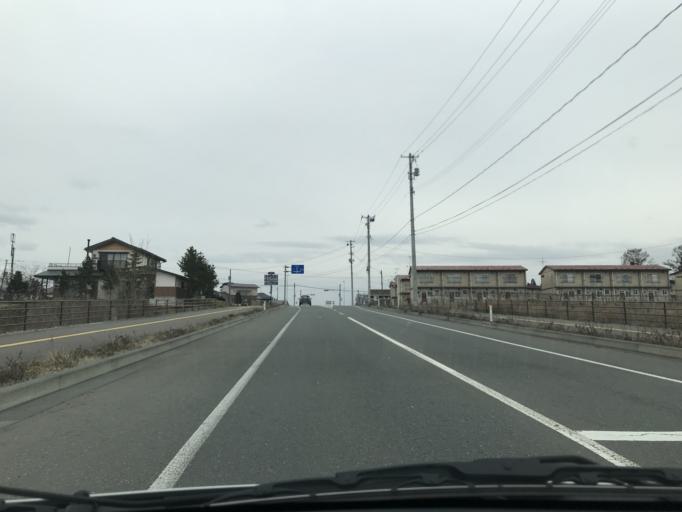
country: JP
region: Iwate
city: Hanamaki
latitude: 39.3715
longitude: 141.1119
